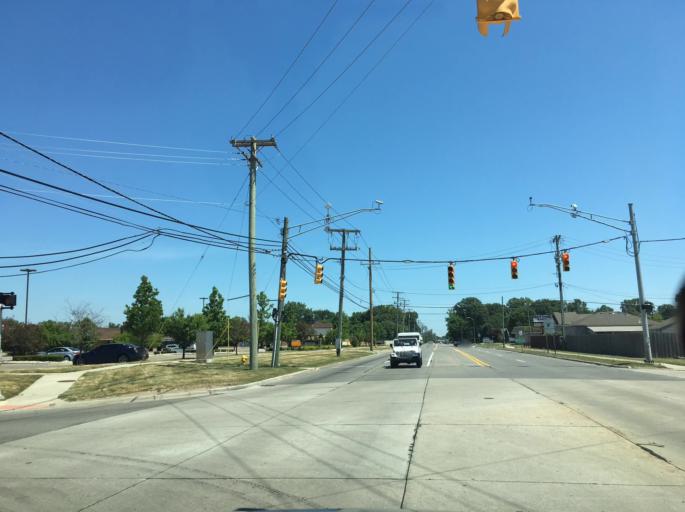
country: US
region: Michigan
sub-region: Macomb County
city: Saint Clair Shores
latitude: 42.5401
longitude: -82.8821
